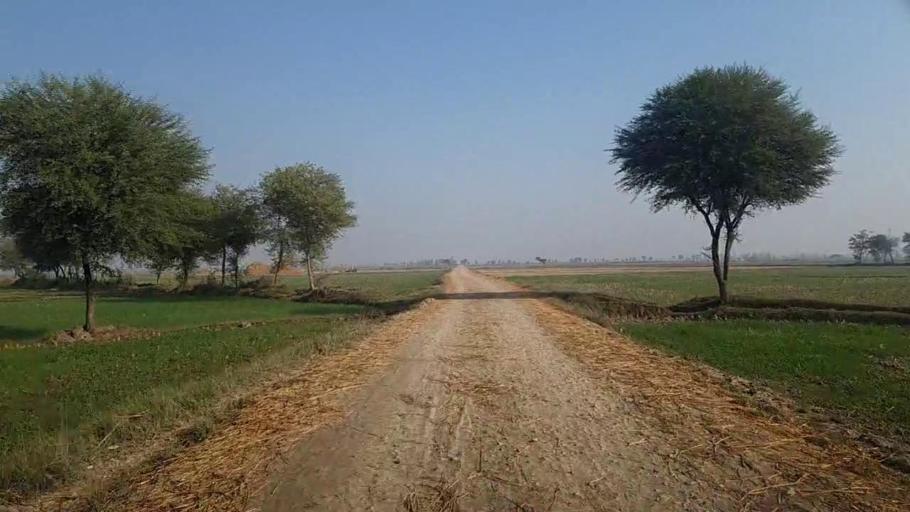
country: PK
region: Sindh
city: Radhan
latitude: 27.1207
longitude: 67.8973
